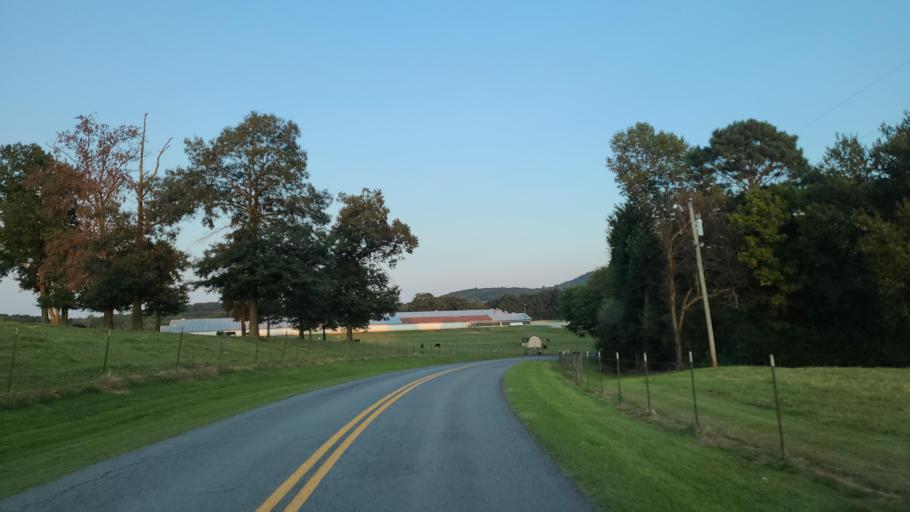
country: US
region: Georgia
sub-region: Pickens County
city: Jasper
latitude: 34.4642
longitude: -84.5306
